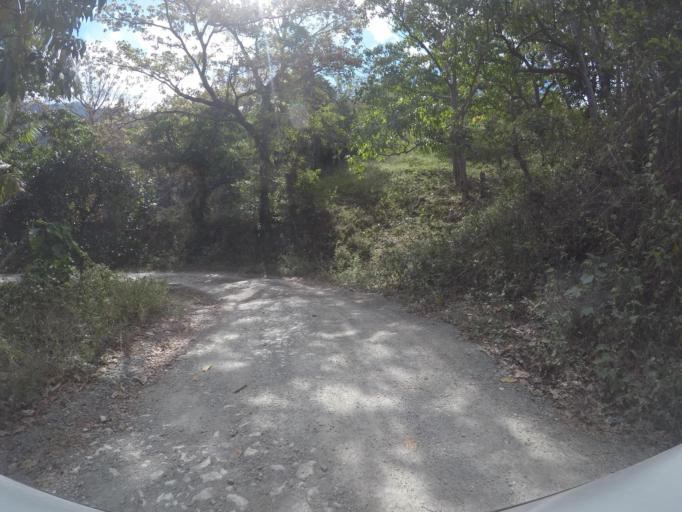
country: TL
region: Baucau
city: Baucau
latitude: -8.6190
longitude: 126.6607
